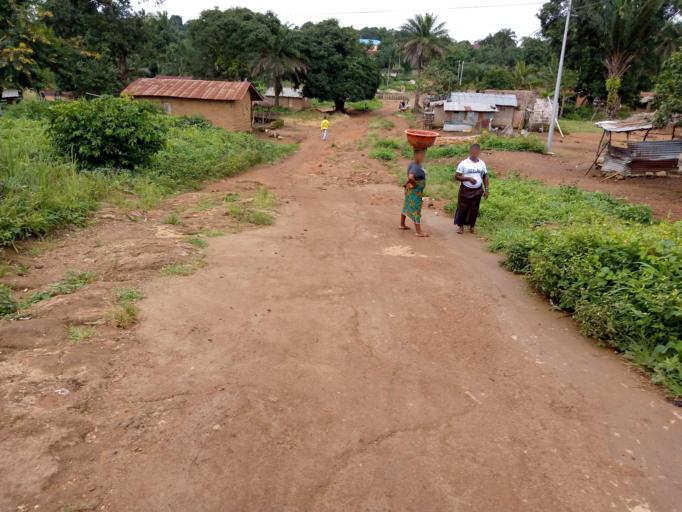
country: SL
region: Eastern Province
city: Buedu
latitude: 8.4577
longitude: -10.3343
